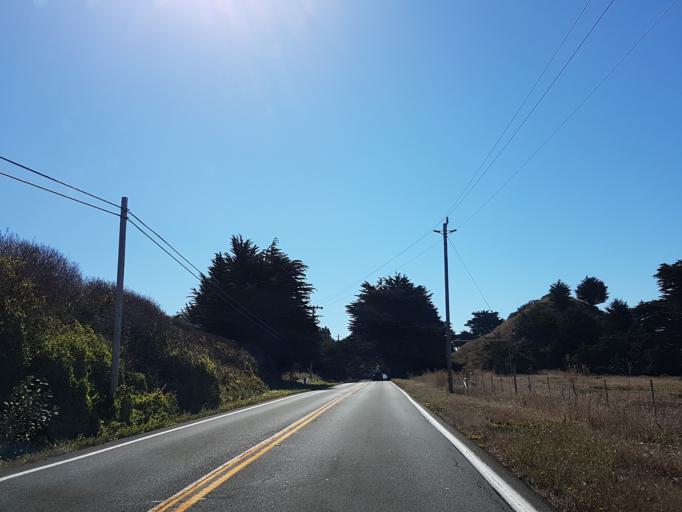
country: US
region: California
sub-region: Mendocino County
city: Boonville
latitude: 39.0952
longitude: -123.7037
